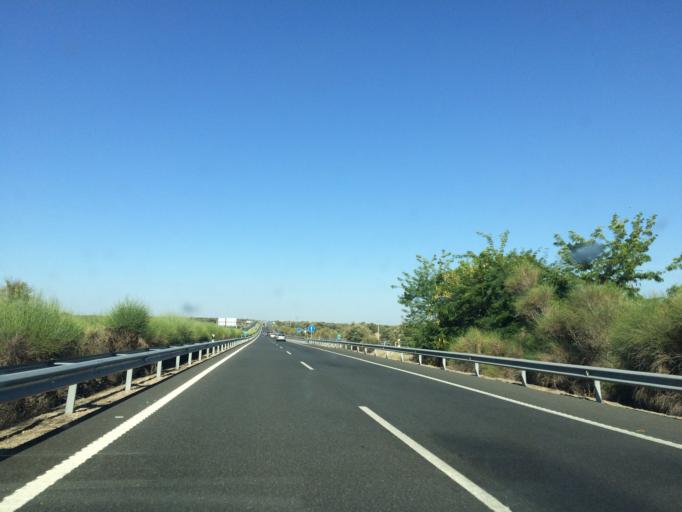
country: ES
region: Extremadura
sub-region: Provincia de Caceres
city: Peraleda de la Mata
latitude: 39.8907
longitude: -5.4307
